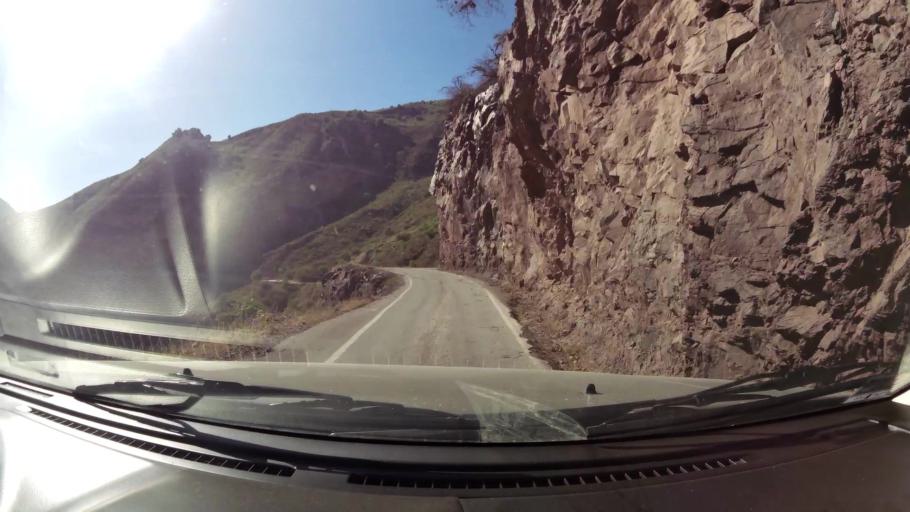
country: PE
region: Huancavelica
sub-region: Provincia de Acobamba
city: Pomacocha
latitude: -12.7894
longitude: -74.4883
